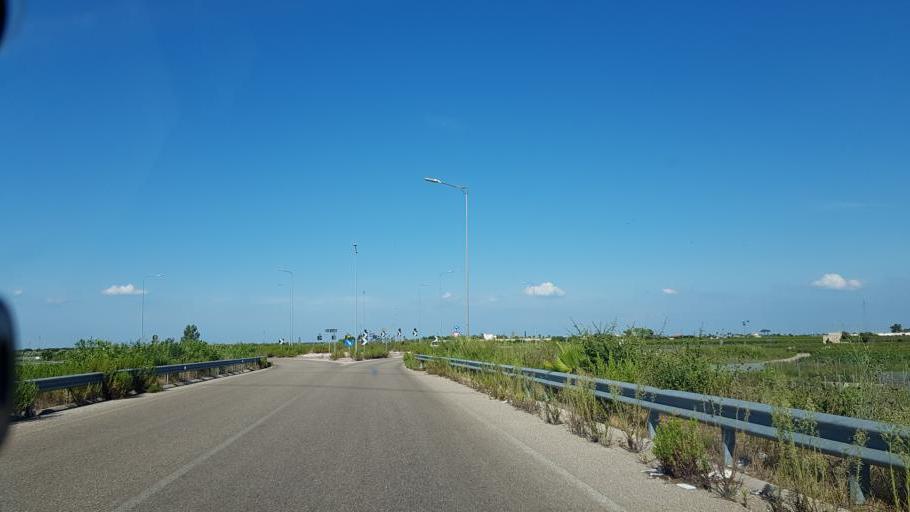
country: IT
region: Apulia
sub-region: Provincia di Lecce
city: Copertino
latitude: 40.2775
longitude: 18.0257
